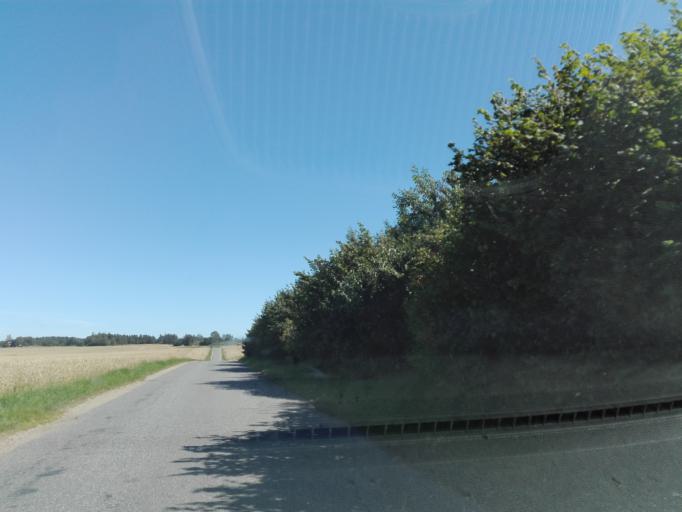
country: DK
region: Central Jutland
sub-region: Arhus Kommune
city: Malling
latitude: 55.9919
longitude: 10.2258
